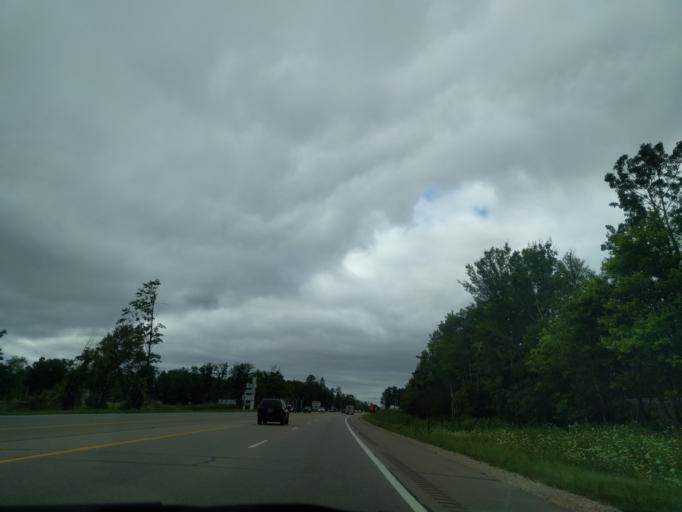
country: US
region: Michigan
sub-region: Delta County
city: Gladstone
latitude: 45.8092
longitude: -87.0599
